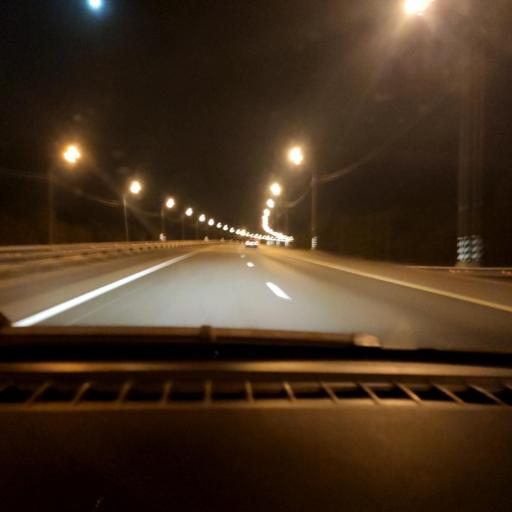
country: RU
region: Lipetsk
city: Khlevnoye
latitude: 52.1845
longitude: 39.1866
